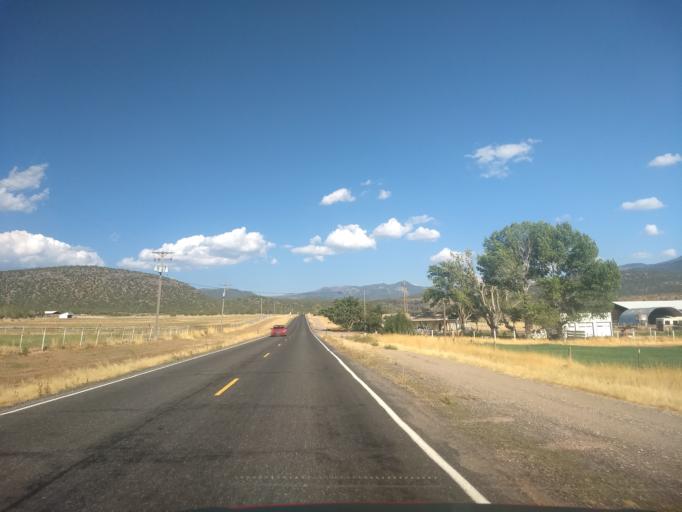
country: US
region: Utah
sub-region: Washington County
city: Enterprise
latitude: 37.4170
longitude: -113.6186
